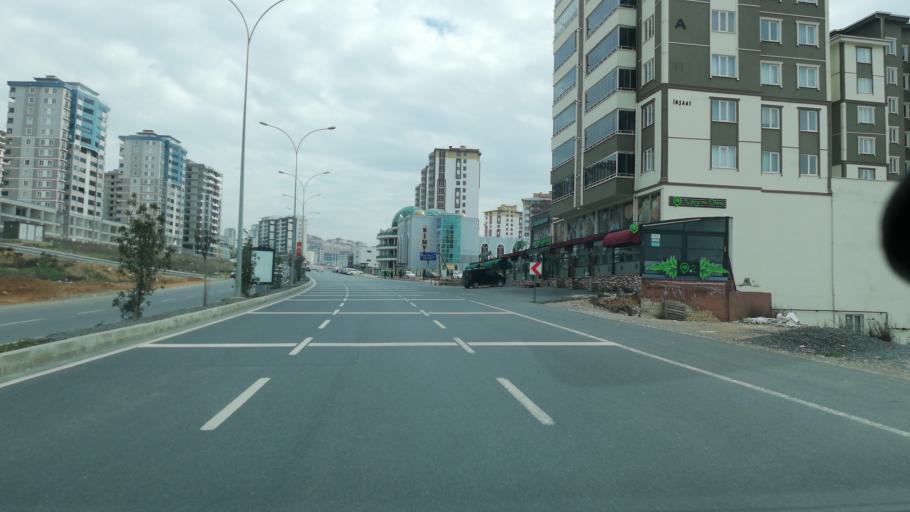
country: TR
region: Kahramanmaras
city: Kahramanmaras
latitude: 37.5862
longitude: 36.8474
